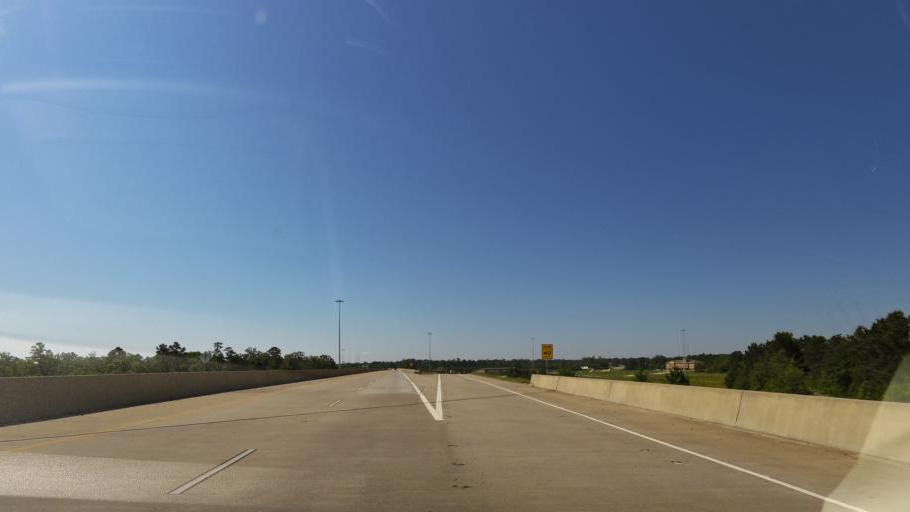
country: US
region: Texas
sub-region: Angelina County
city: Redland
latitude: 31.3753
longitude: -94.7105
